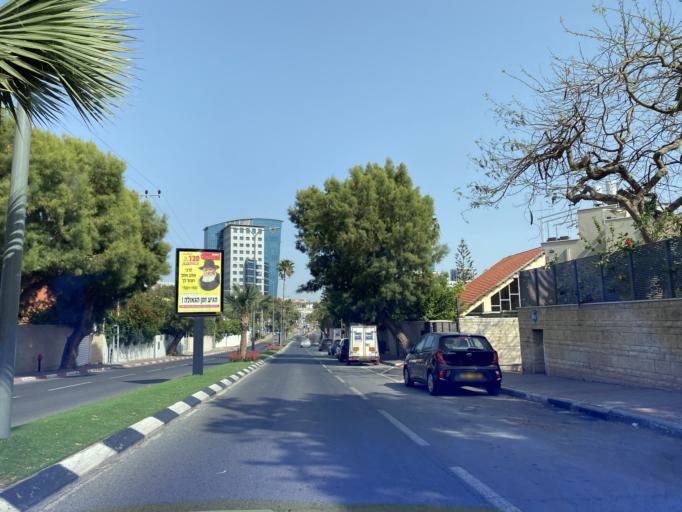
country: IL
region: Tel Aviv
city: Herzliya Pituah
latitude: 32.1674
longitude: 34.8069
